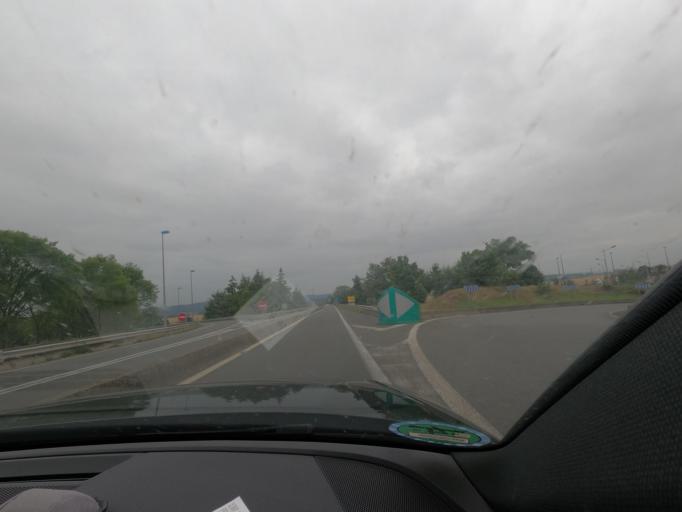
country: FR
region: Picardie
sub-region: Departement de l'Oise
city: Ressons-sur-Matz
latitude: 49.5215
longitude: 2.7182
